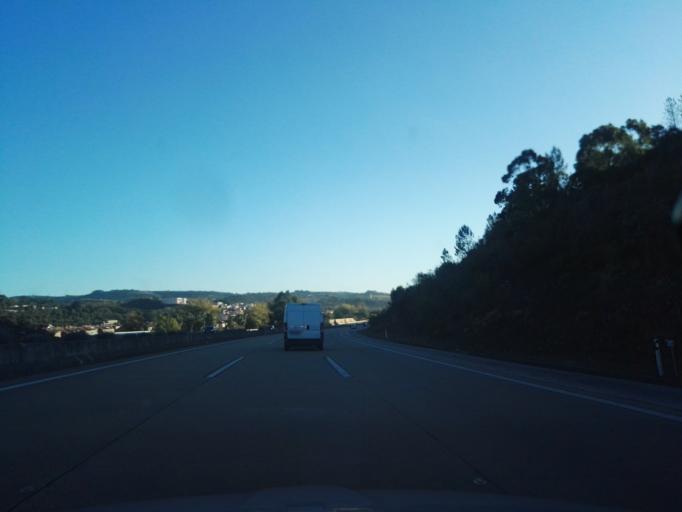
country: PT
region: Lisbon
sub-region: Loures
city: Bucelas
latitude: 38.8978
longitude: -9.1132
